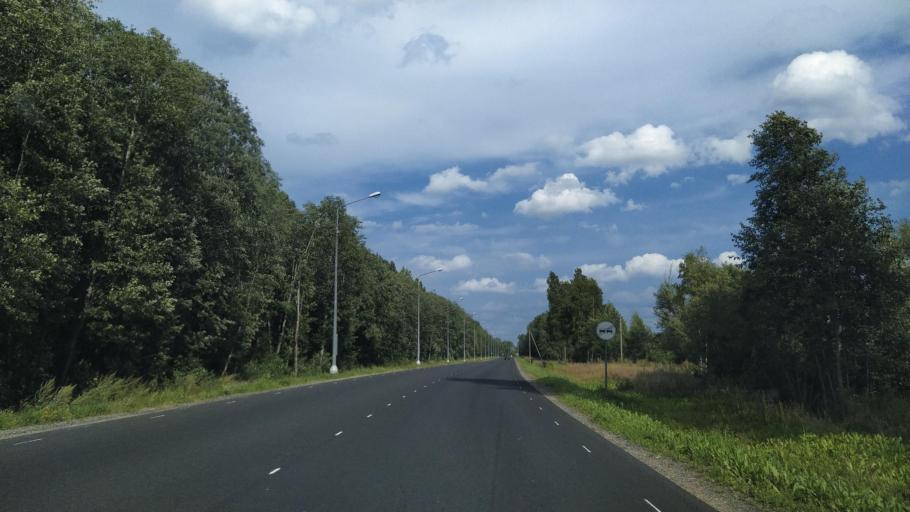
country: RU
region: Pskov
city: Vybor
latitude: 57.7273
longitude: 28.9630
